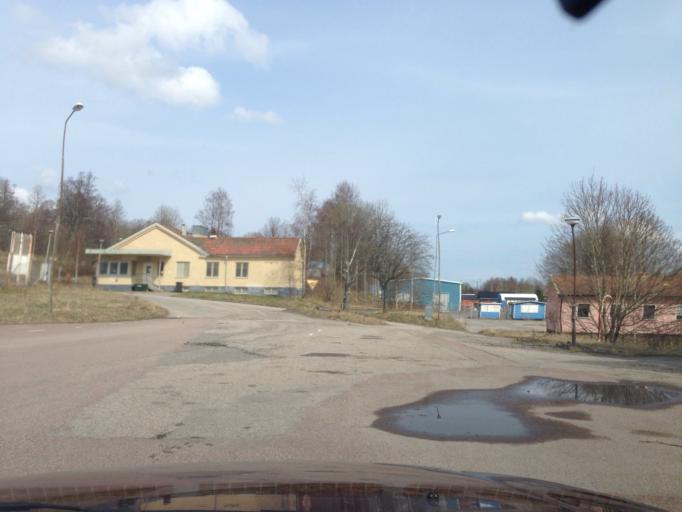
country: SE
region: Dalarna
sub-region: Ludvika Kommun
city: Grangesberg
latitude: 60.0766
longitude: 14.9873
